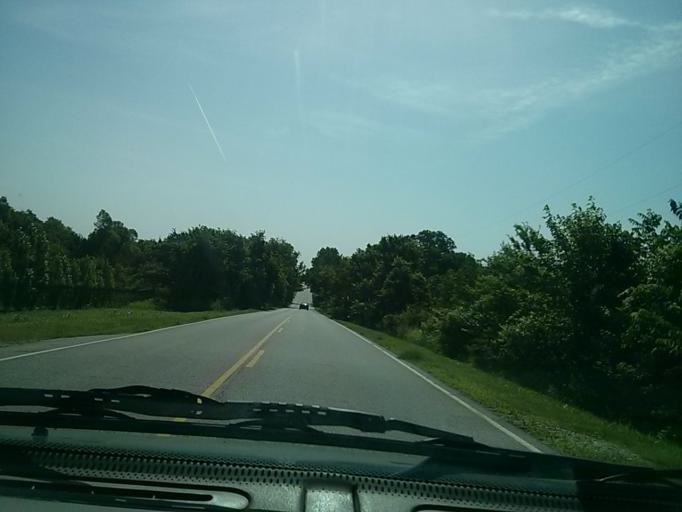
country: US
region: Oklahoma
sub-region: Rogers County
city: Catoosa
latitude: 36.1335
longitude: -95.7963
